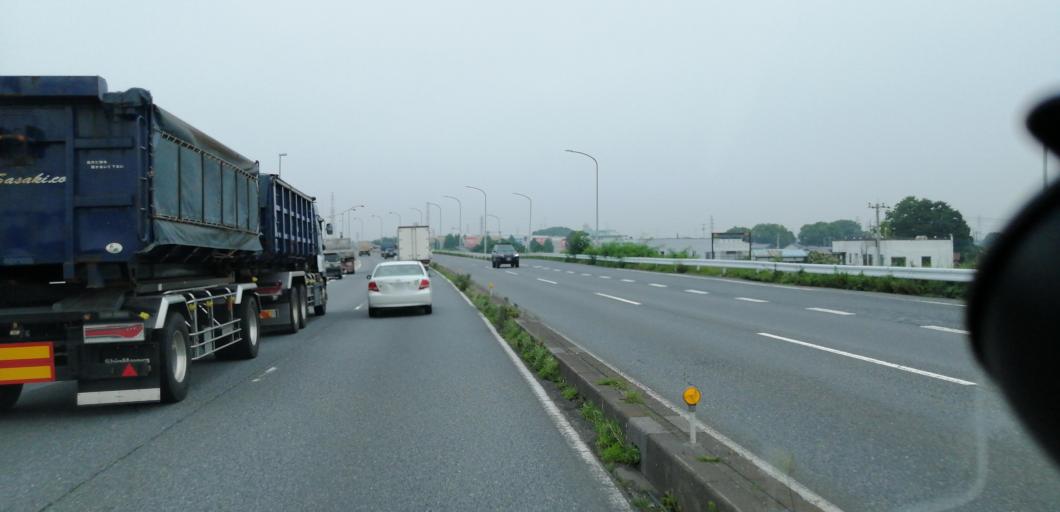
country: JP
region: Saitama
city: Kumagaya
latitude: 36.1716
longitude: 139.3744
